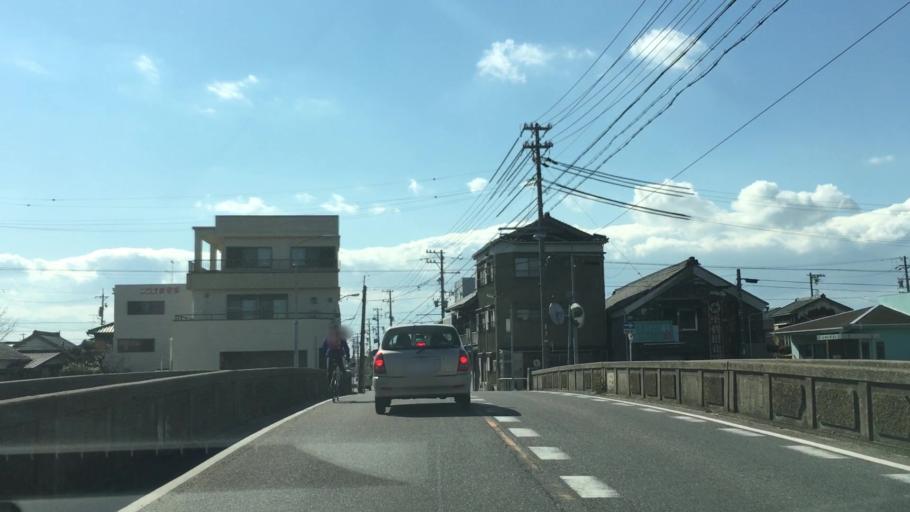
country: JP
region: Aichi
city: Ishiki
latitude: 34.7959
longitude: 137.0739
